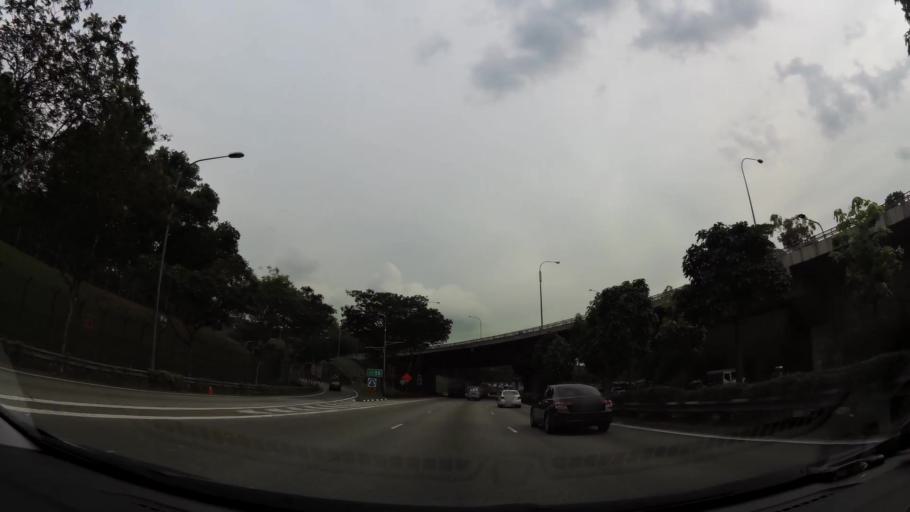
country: MY
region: Johor
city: Johor Bahru
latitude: 1.4150
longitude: 103.8054
